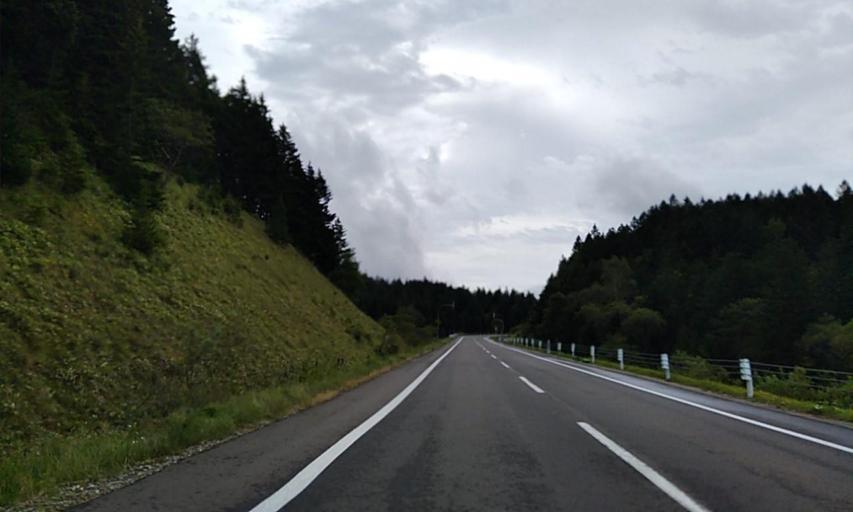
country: JP
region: Hokkaido
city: Abashiri
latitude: 43.6253
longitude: 144.5771
